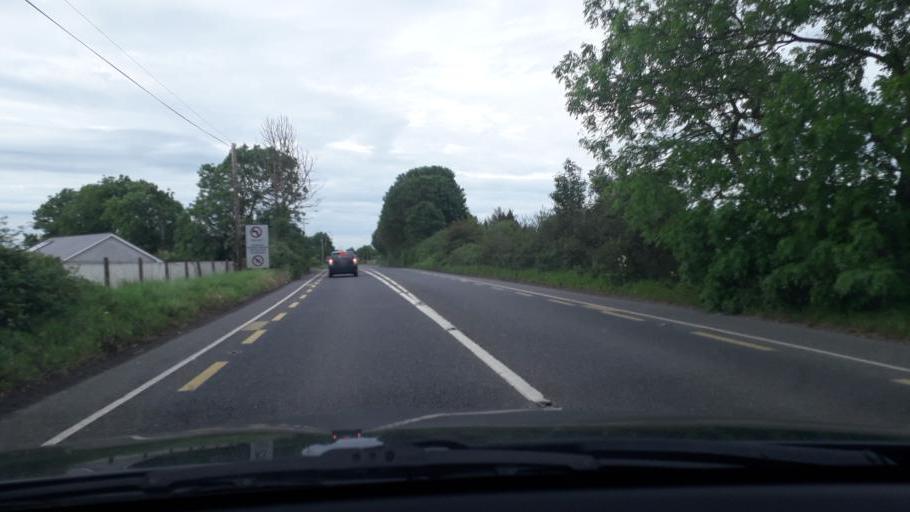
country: IE
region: Leinster
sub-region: County Carlow
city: Carlow
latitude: 52.7814
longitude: -6.9510
